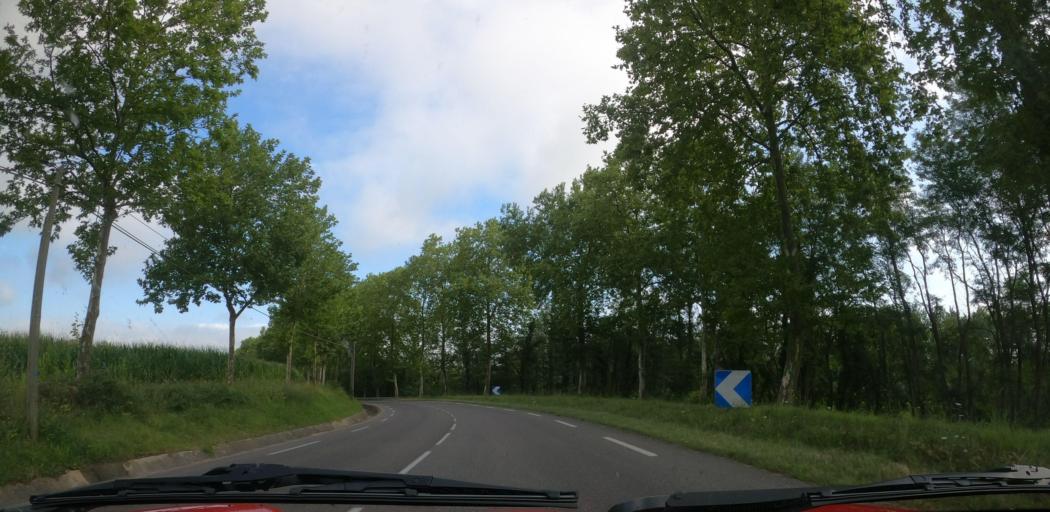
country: FR
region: Aquitaine
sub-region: Departement des Landes
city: Peyrehorade
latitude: 43.5263
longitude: -1.1037
